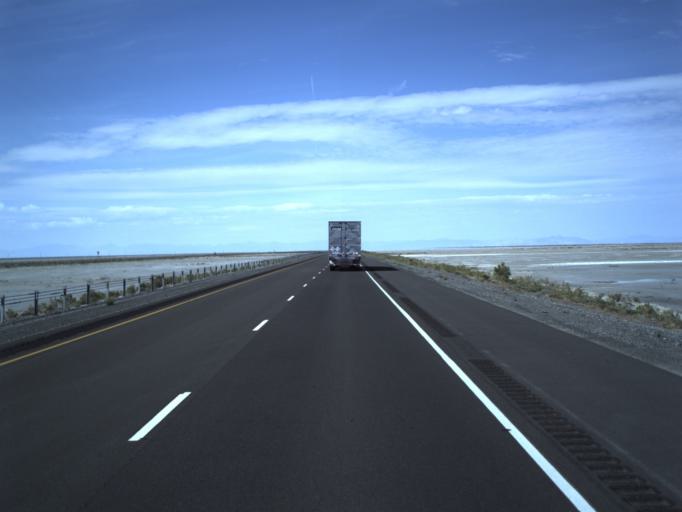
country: US
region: Utah
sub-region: Tooele County
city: Wendover
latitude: 40.7286
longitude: -113.3454
